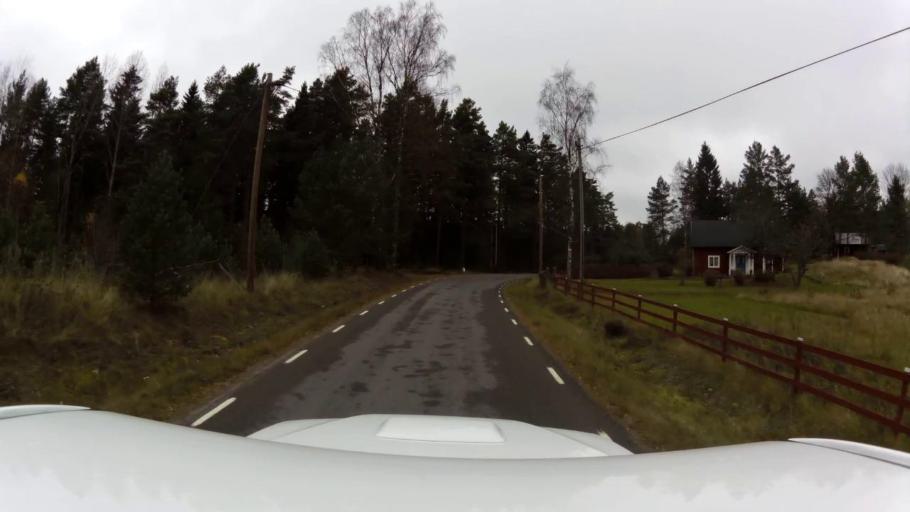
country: SE
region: OEstergoetland
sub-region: Kinda Kommun
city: Kisa
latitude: 58.1336
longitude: 15.4527
